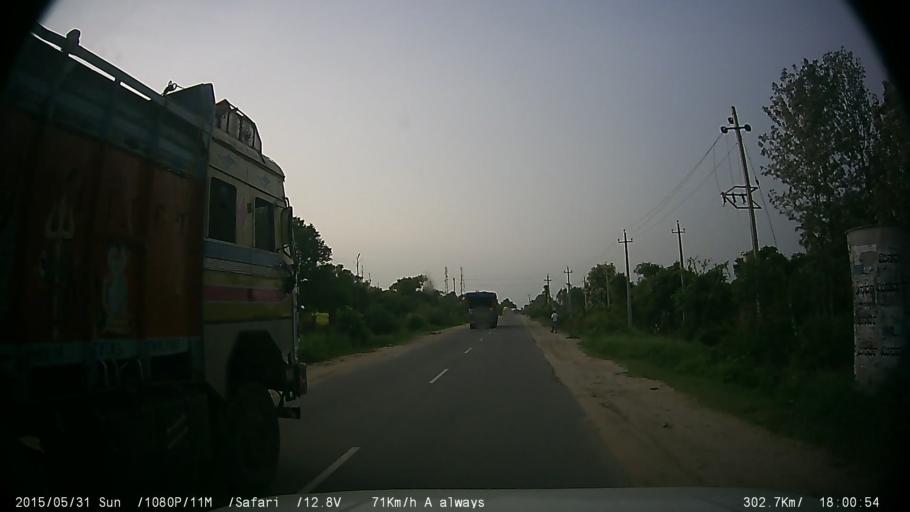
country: IN
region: Karnataka
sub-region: Mysore
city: Nanjangud
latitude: 12.0251
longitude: 76.6734
